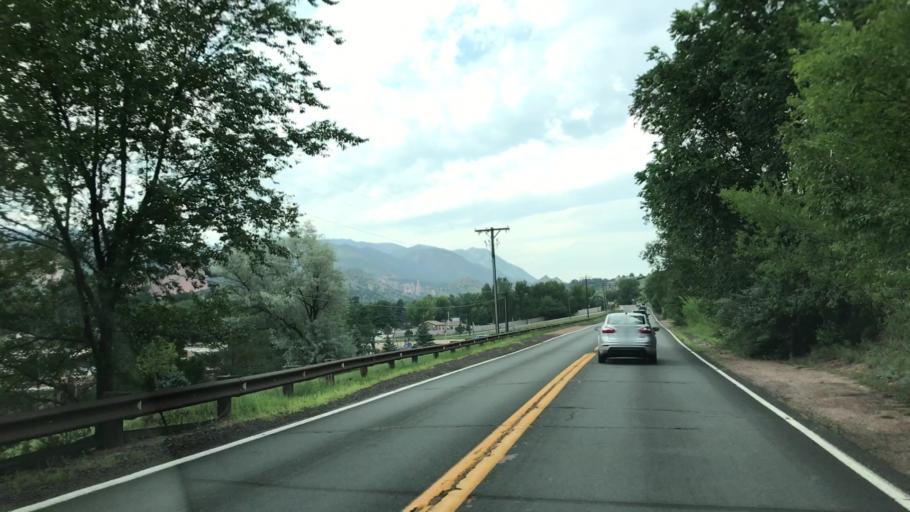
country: US
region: Colorado
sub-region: El Paso County
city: Manitou Springs
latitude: 38.8648
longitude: -104.8665
